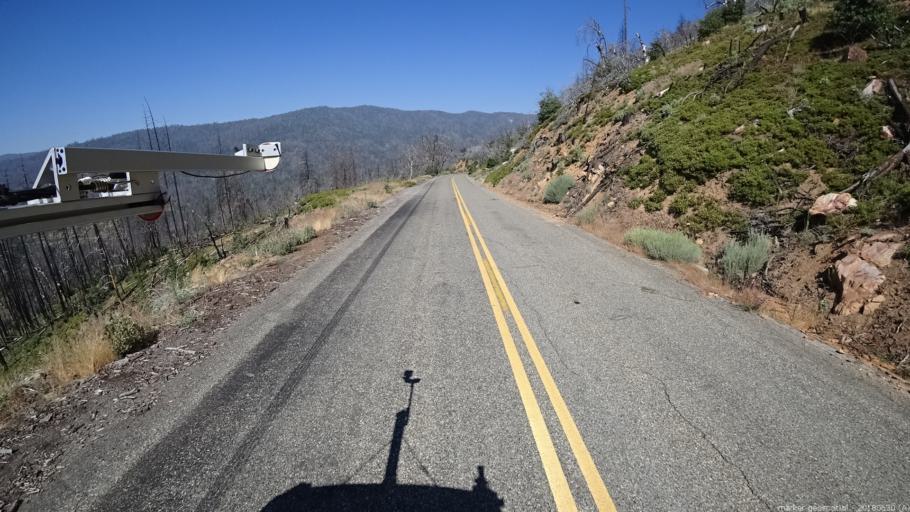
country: US
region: California
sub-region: Fresno County
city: Auberry
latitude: 37.2961
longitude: -119.3486
